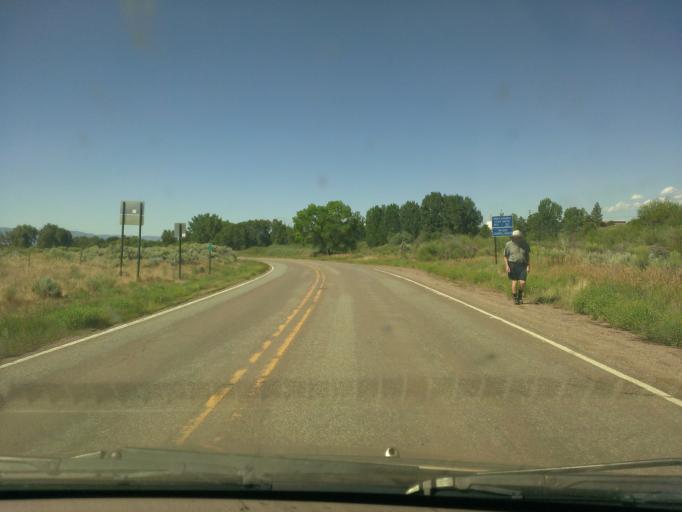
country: US
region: New Mexico
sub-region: Taos County
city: Arroyo Seco
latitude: 36.5003
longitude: -105.5918
